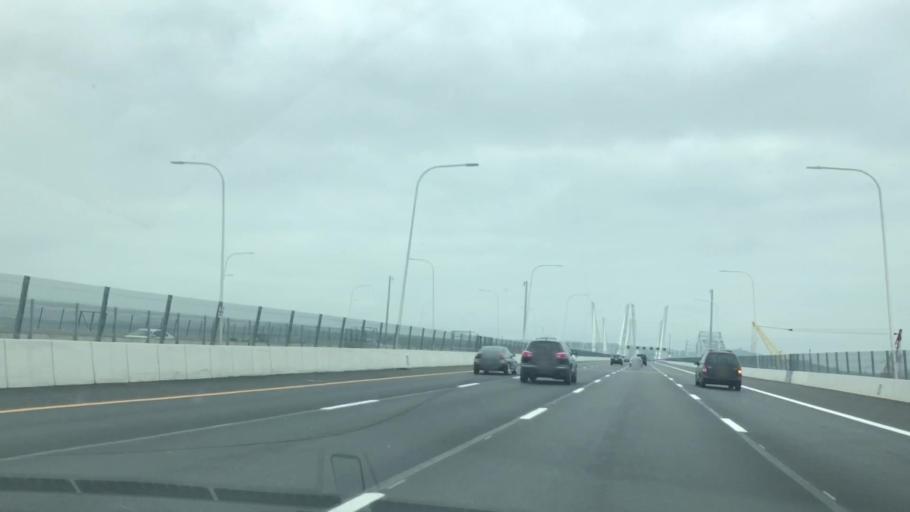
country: US
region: New York
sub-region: Rockland County
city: South Nyack
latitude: 41.0710
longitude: -73.8986
